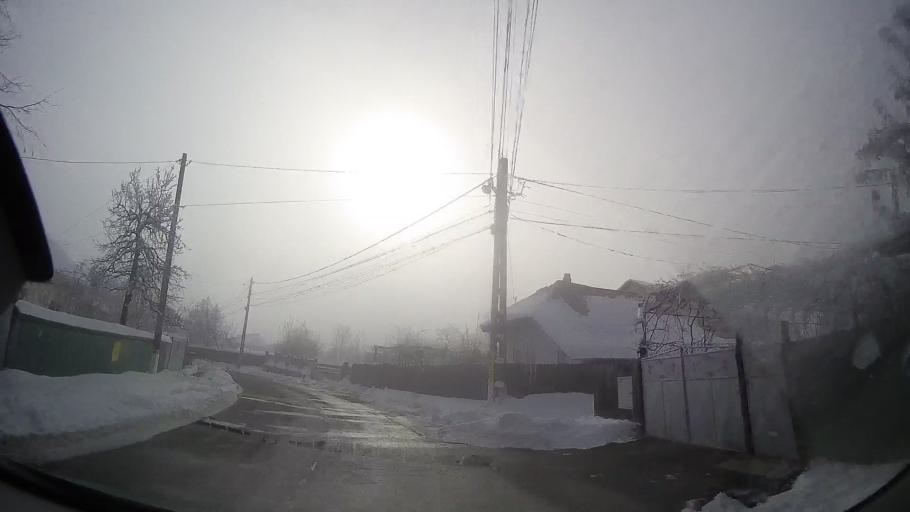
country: RO
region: Iasi
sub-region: Comuna Valea Seaca
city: Topile
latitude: 47.2437
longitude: 26.6651
